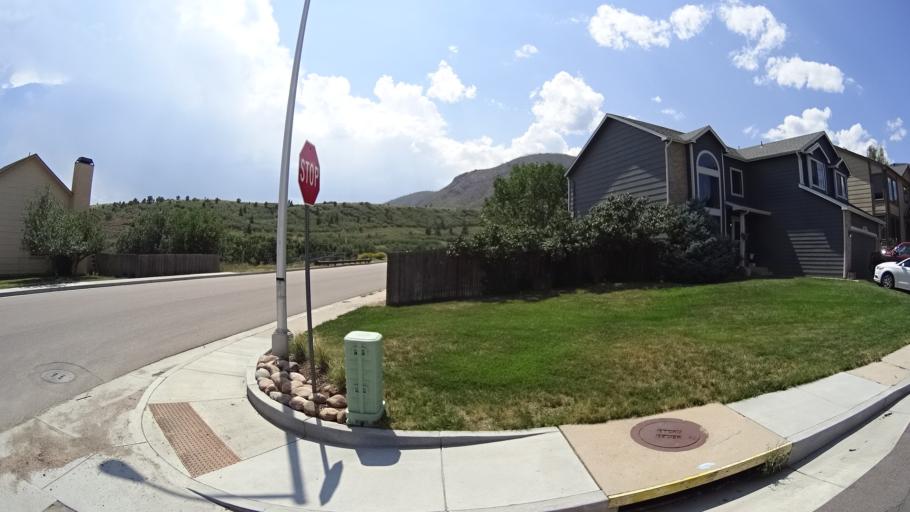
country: US
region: Colorado
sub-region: El Paso County
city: Air Force Academy
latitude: 38.9364
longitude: -104.8792
